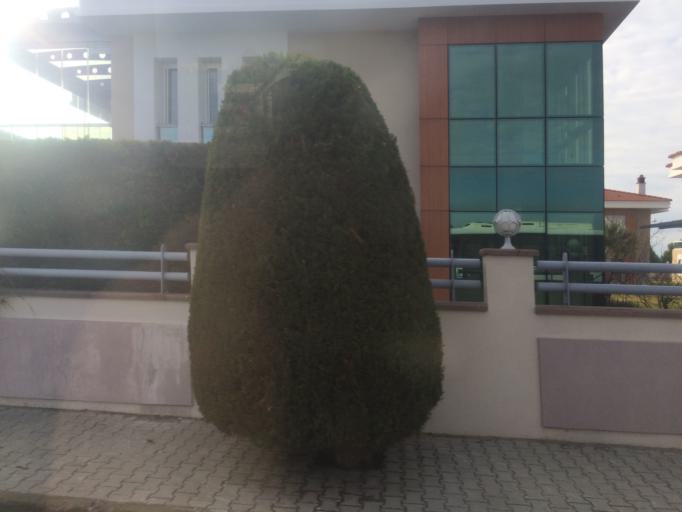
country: TR
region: Izmir
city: Menemen
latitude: 38.5072
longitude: 26.9581
